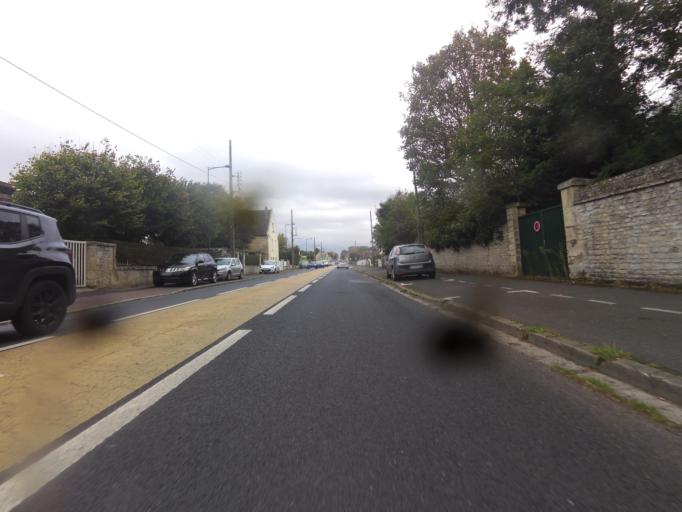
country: FR
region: Lower Normandy
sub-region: Departement du Calvados
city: Bretteville-sur-Odon
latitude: 49.1669
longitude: -0.4125
